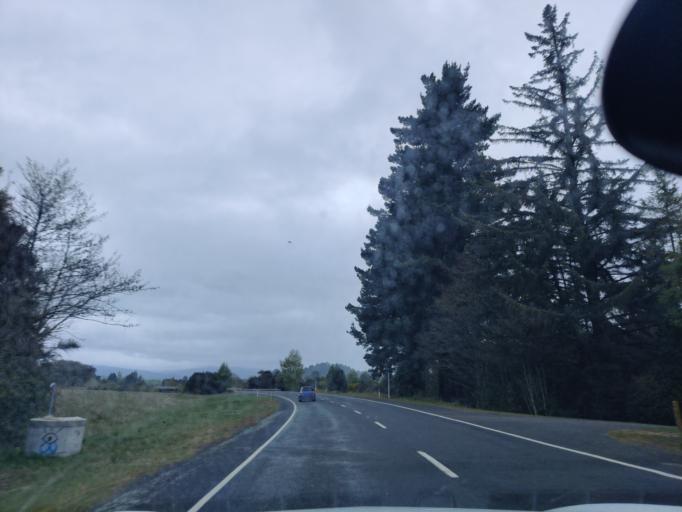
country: NZ
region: Waikato
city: Turangi
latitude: -38.9772
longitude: 175.7720
